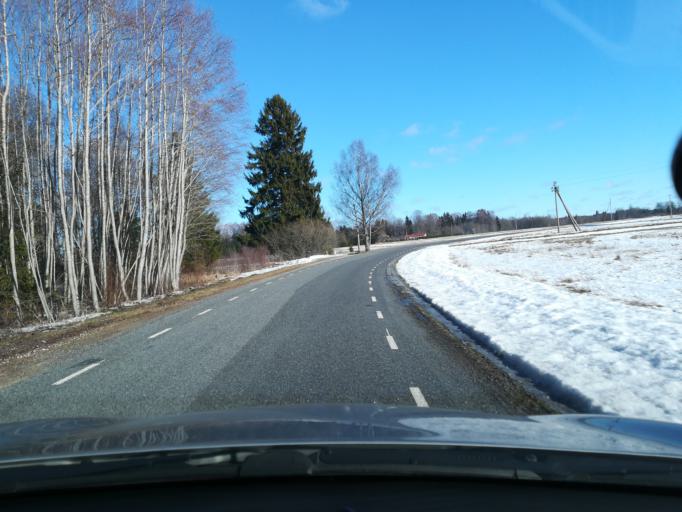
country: EE
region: Raplamaa
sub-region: Kohila vald
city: Kohila
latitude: 59.2295
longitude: 24.7338
